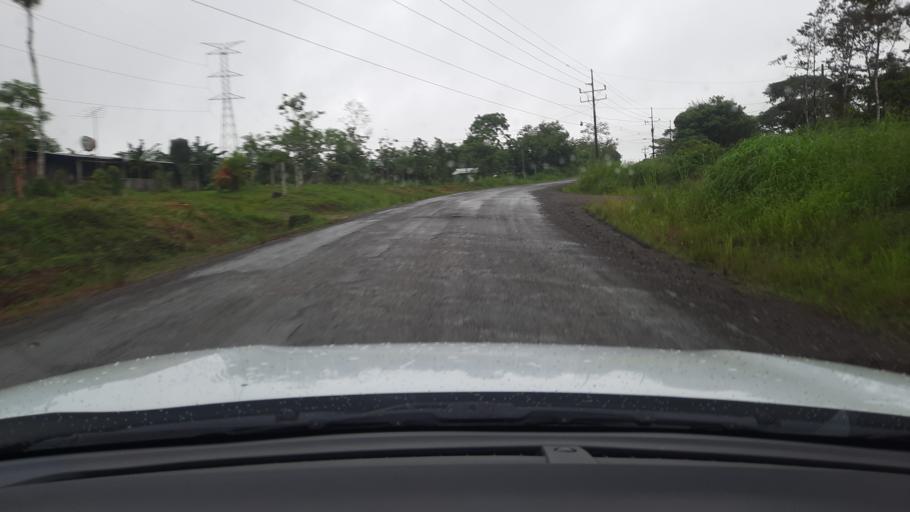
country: NI
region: Rivas
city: Cardenas
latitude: 11.0306
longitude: -85.3656
